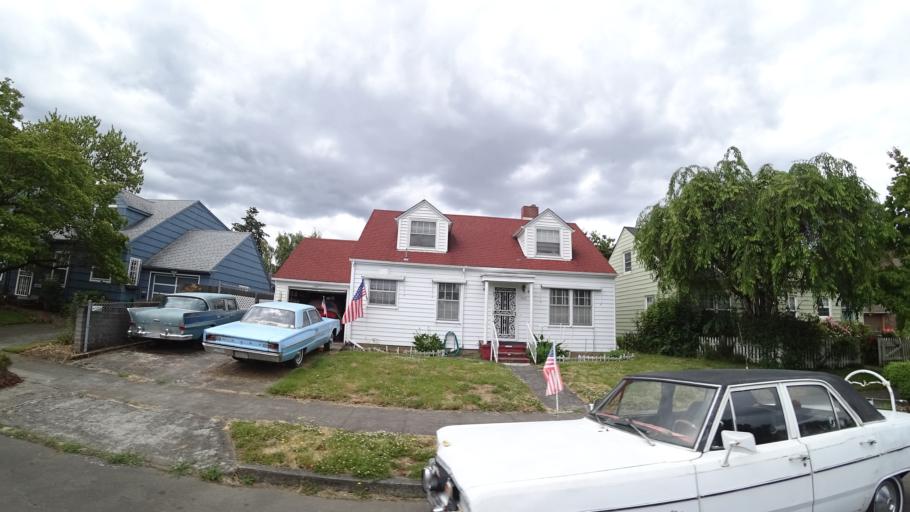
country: US
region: Oregon
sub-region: Multnomah County
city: Portland
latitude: 45.5765
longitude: -122.7100
